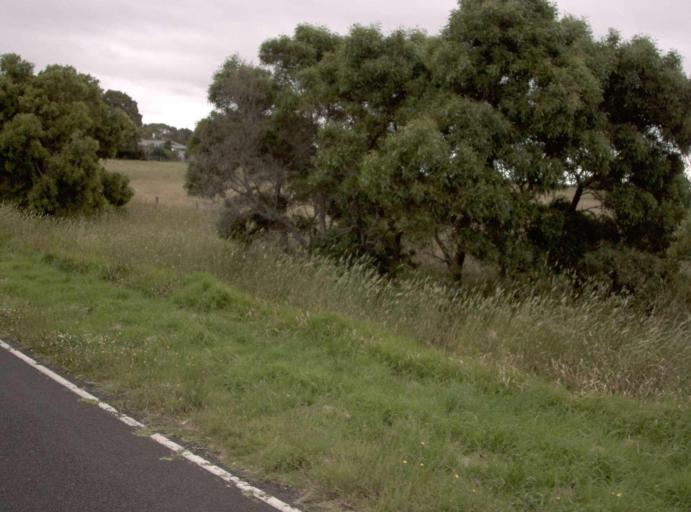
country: AU
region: Victoria
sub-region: Wellington
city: Sale
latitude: -38.5392
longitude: 146.8882
